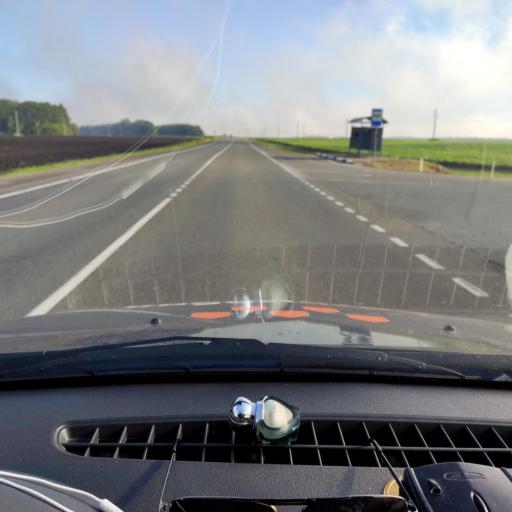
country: RU
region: Orjol
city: Pokrovskoye
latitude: 52.5329
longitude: 37.0431
